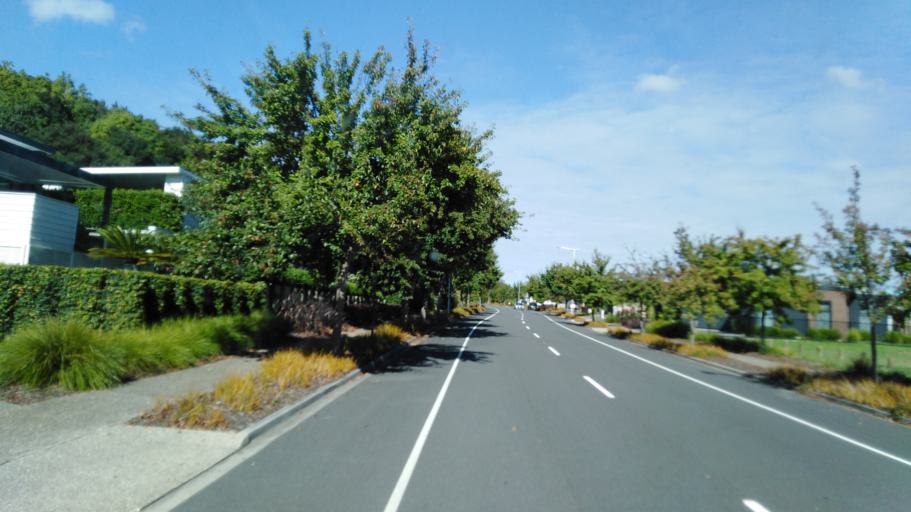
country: NZ
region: Bay of Plenty
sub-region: Tauranga City
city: Tauranga
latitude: -37.7499
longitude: 176.1081
